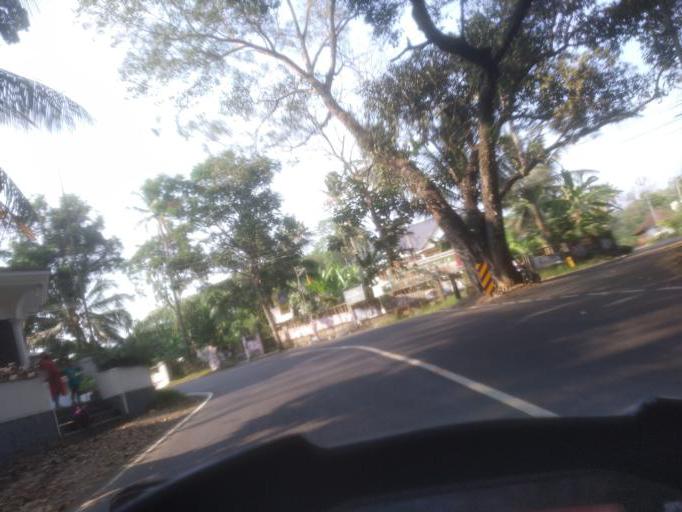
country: IN
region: Kerala
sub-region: Ernakulam
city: Piravam
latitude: 9.8314
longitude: 76.5094
